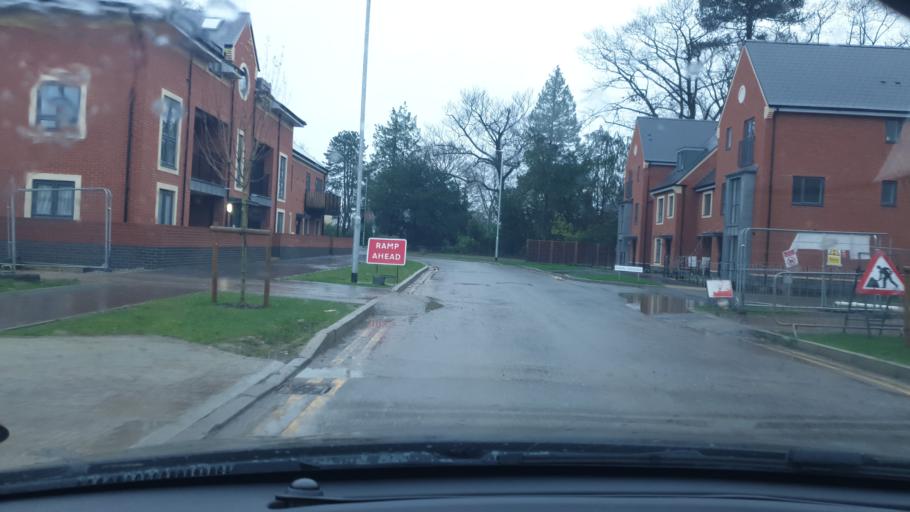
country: GB
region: England
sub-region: Essex
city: Great Horkesley
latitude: 51.9194
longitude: 0.8941
